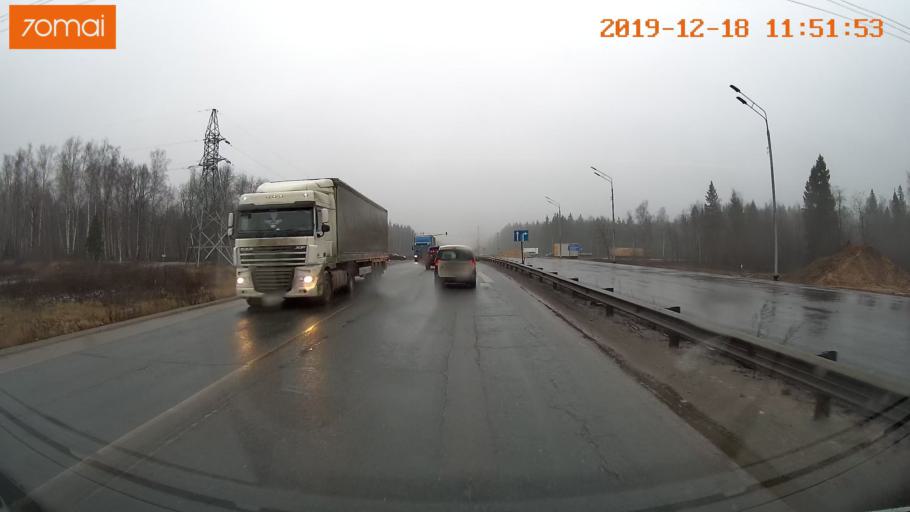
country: RU
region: Moskovskaya
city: Yershovo
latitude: 55.7966
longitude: 36.9212
